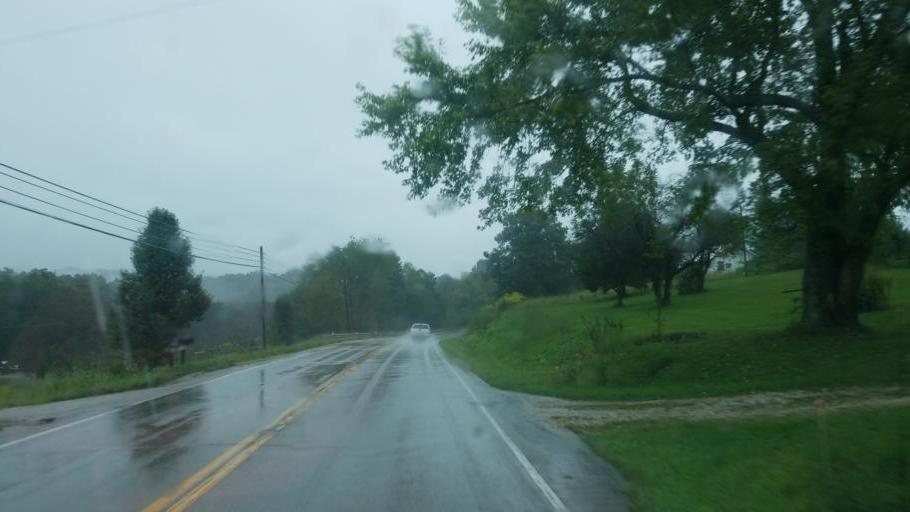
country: US
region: Kentucky
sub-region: Rowan County
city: Morehead
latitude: 38.2151
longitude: -83.4806
